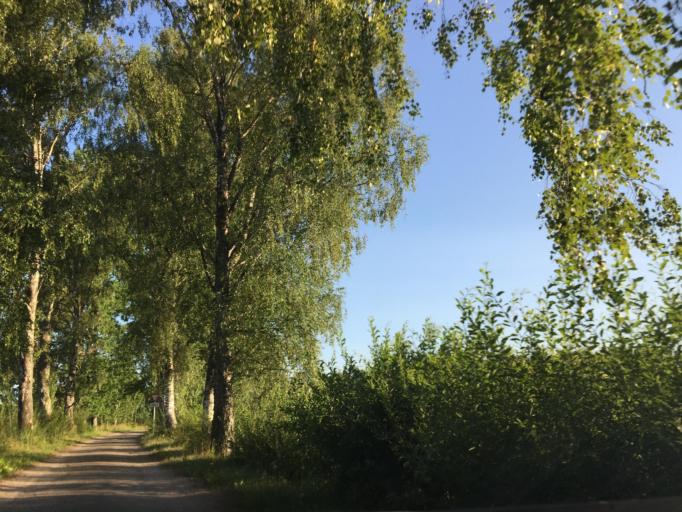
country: LV
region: Talsu Rajons
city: Stende
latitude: 57.1581
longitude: 22.2934
